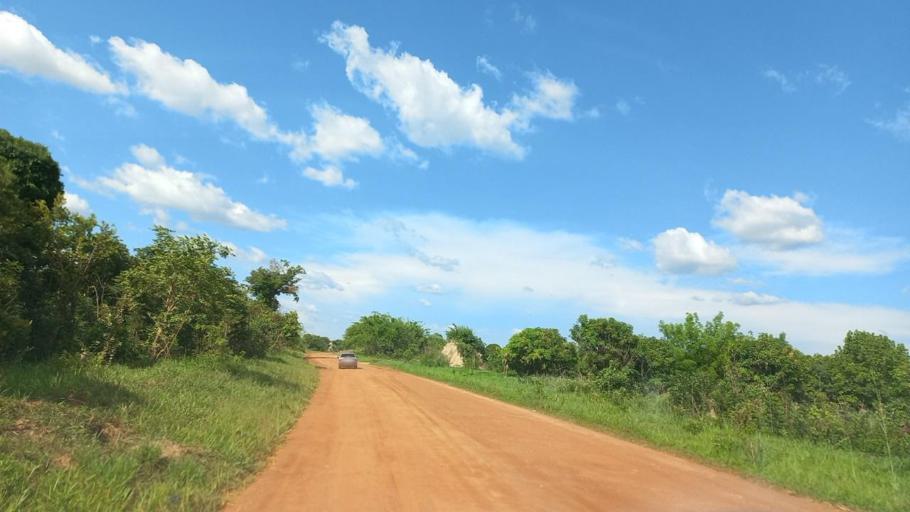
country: ZM
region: Copperbelt
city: Kitwe
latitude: -12.8598
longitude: 28.3839
